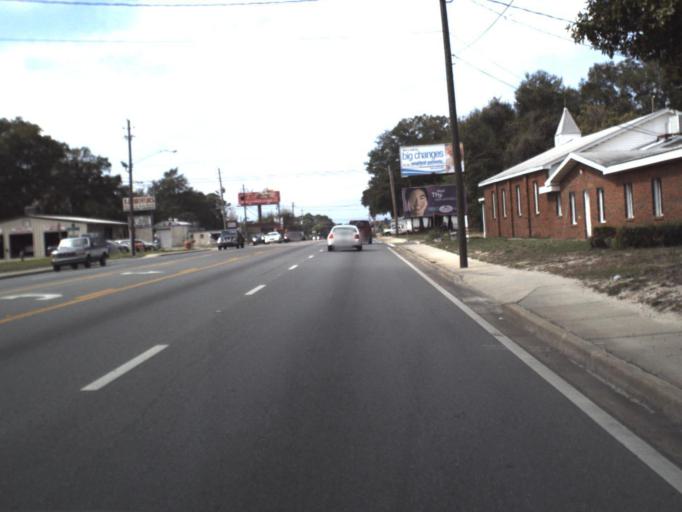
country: US
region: Florida
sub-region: Bay County
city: Pretty Bayou
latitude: 30.1754
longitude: -85.6893
